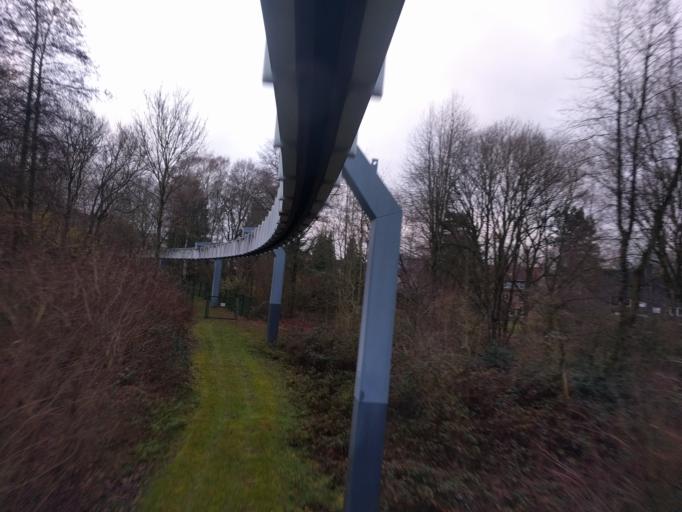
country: DE
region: North Rhine-Westphalia
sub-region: Regierungsbezirk Arnsberg
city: Dortmund
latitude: 51.4839
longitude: 7.4096
